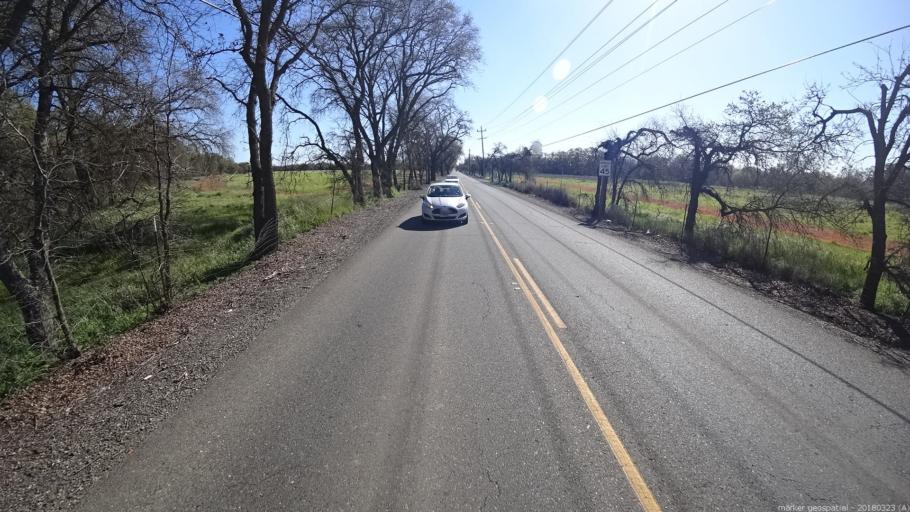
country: US
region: California
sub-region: Sacramento County
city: Rio Linda
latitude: 38.6981
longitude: -121.4288
